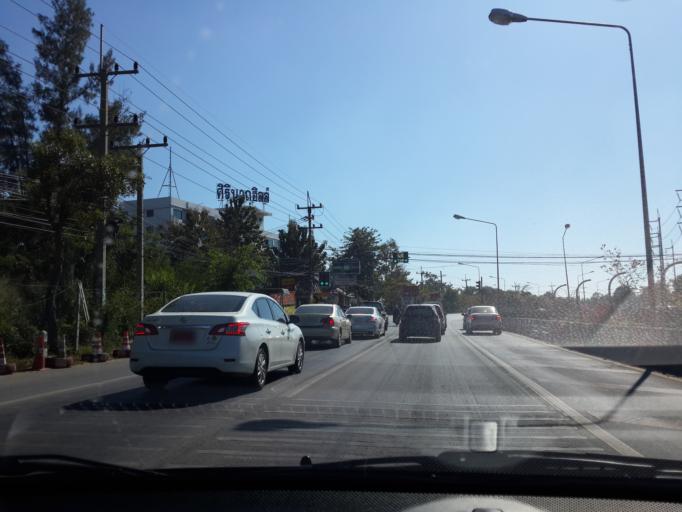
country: TH
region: Chiang Mai
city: Chiang Mai
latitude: 18.7697
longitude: 98.9505
